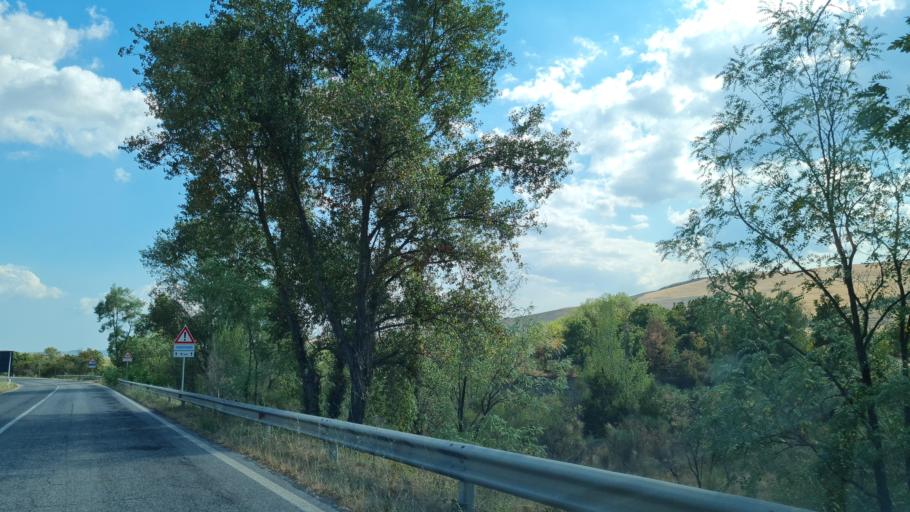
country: IT
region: Tuscany
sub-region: Provincia di Siena
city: Radicofani
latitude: 42.8693
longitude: 11.7419
